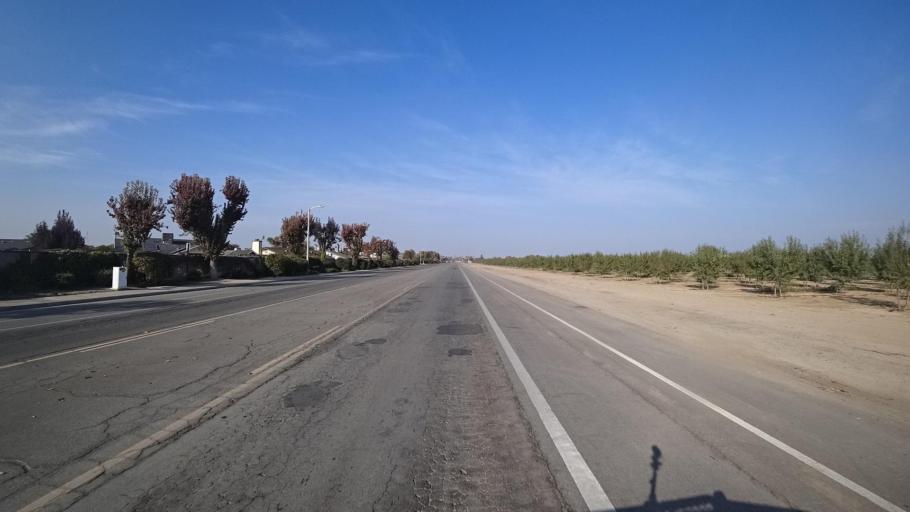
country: US
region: California
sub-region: Kern County
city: Delano
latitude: 35.7795
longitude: -119.2231
